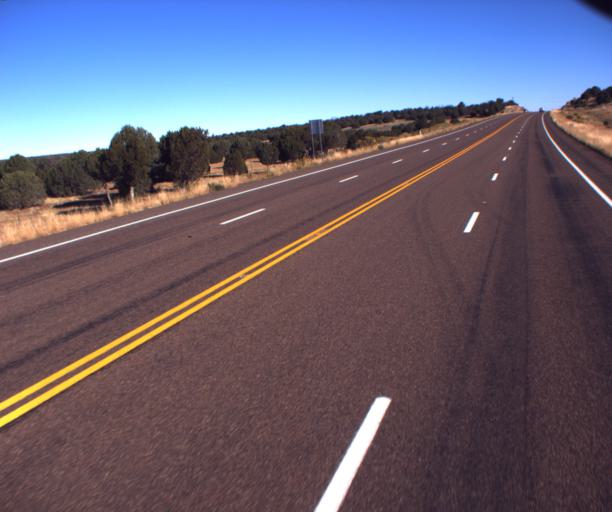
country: US
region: Arizona
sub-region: Navajo County
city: White Mountain Lake
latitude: 34.3620
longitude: -110.0528
